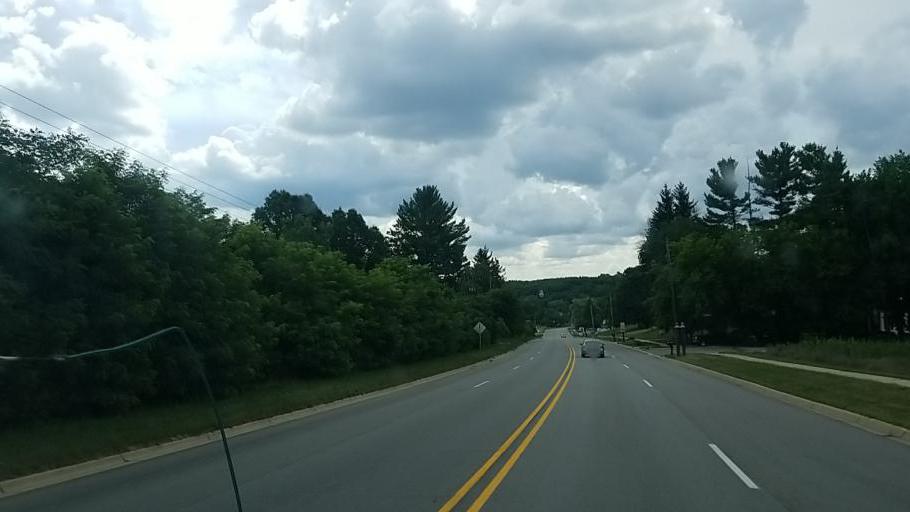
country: US
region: Michigan
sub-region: Kent County
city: Walker
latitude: 43.0054
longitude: -85.7206
